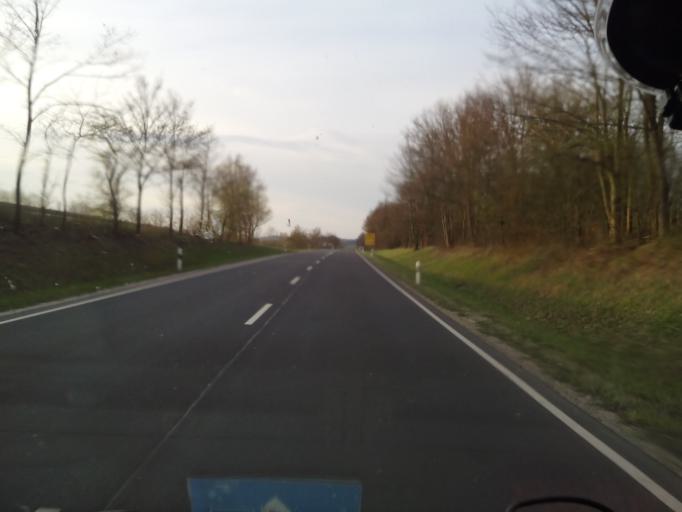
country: DE
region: Bavaria
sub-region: Regierungsbezirk Unterfranken
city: Pfarrweisach
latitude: 50.1225
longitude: 10.7621
